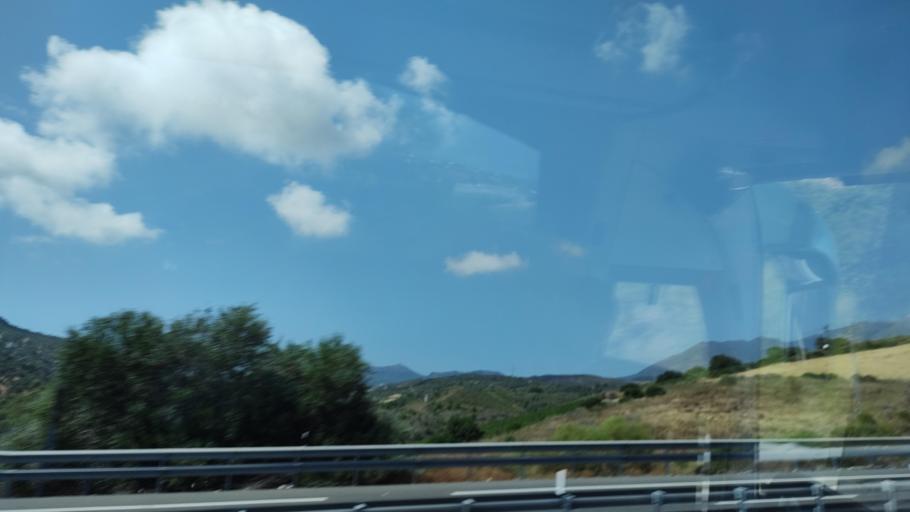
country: ES
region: Andalusia
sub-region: Provincia de Malaga
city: Manilva
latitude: 36.3902
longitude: -5.2575
